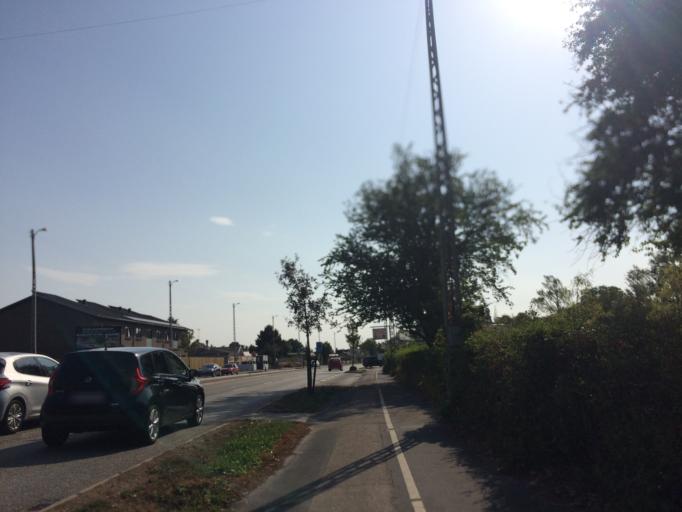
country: DK
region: Capital Region
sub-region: Ishoj Kommune
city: Ishoj
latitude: 55.5948
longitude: 12.3438
